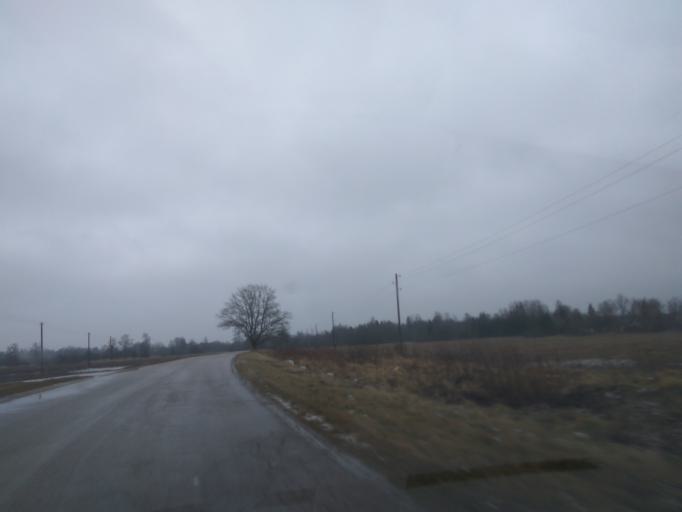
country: LV
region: Broceni
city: Broceni
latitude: 56.8468
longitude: 22.3826
